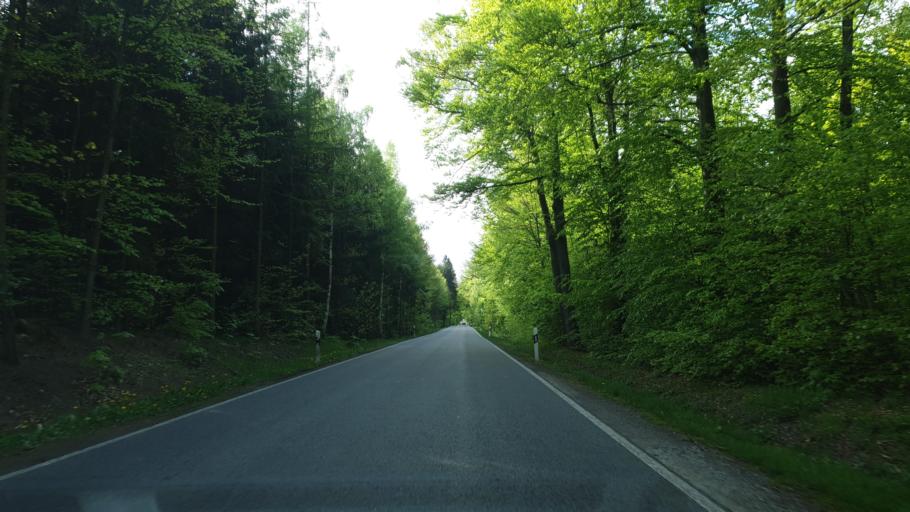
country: DE
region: Saxony
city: Lichtenstein
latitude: 50.7197
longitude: 12.6500
